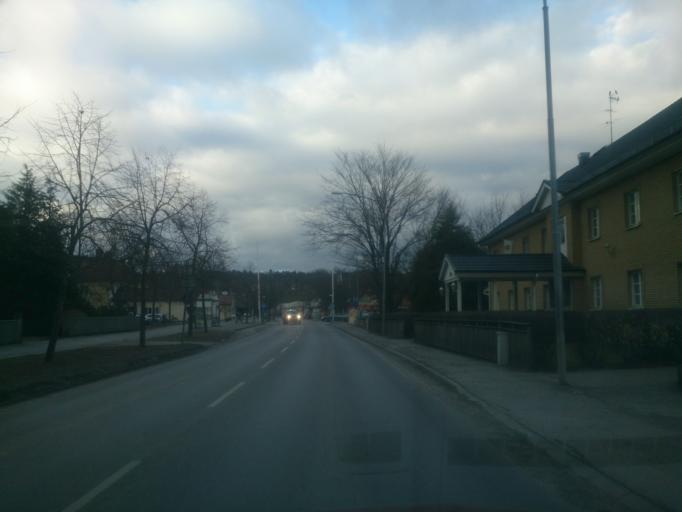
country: SE
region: OEstergoetland
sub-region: Norrkopings Kommun
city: Jursla
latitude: 58.6637
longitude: 16.1805
